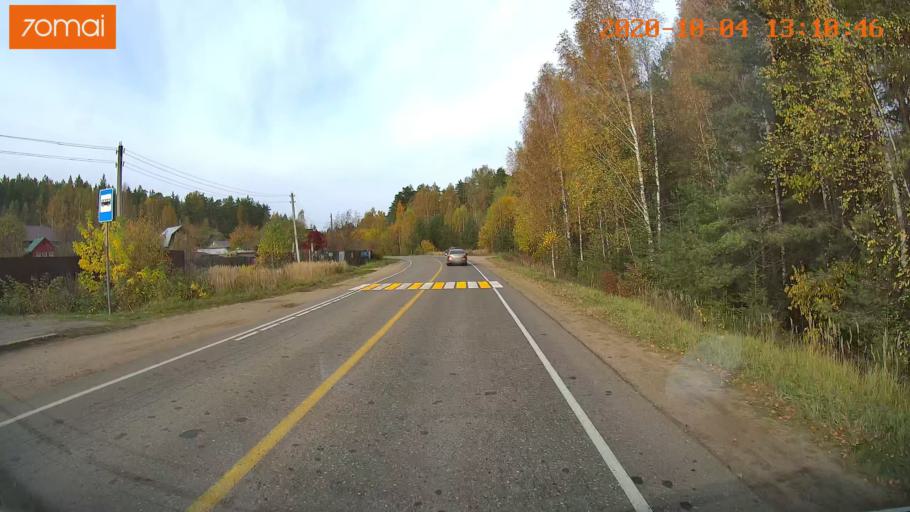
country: RU
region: Ivanovo
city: Bogorodskoye
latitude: 57.0718
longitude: 40.9507
